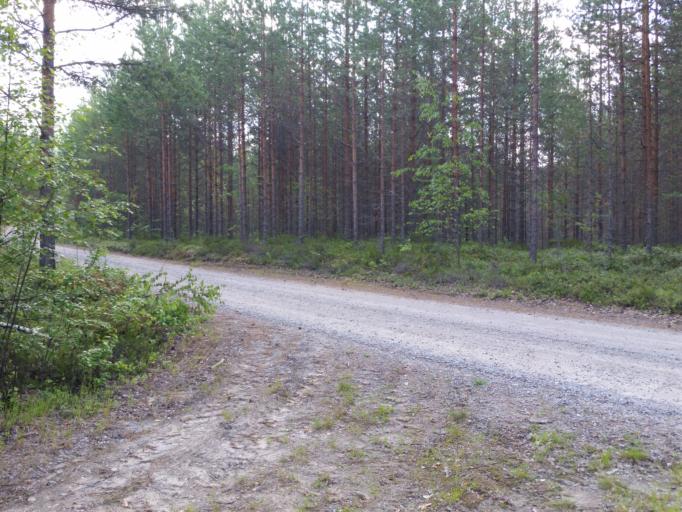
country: FI
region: Southern Savonia
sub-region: Savonlinna
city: Sulkava
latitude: 61.7631
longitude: 28.4325
